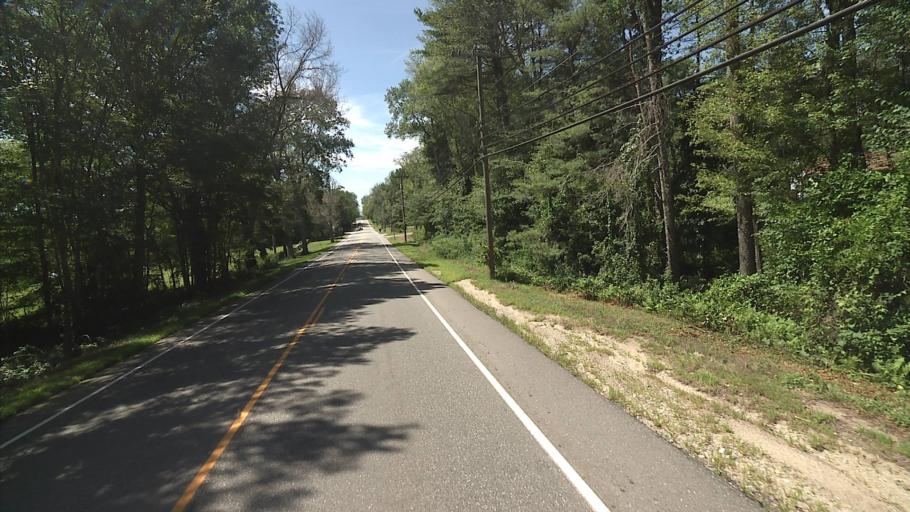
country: US
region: Connecticut
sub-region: Windham County
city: Killingly Center
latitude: 41.8424
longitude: -71.8430
